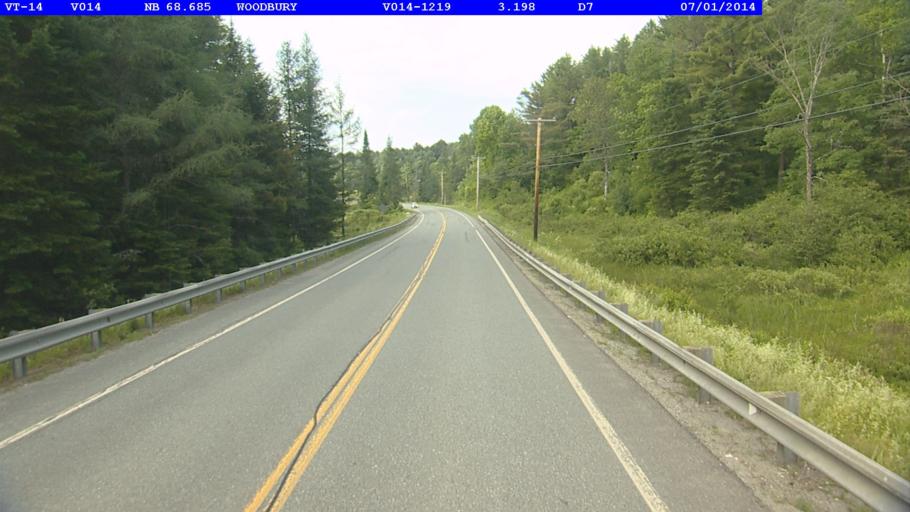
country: US
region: Vermont
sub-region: Caledonia County
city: Hardwick
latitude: 44.4343
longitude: -72.4134
